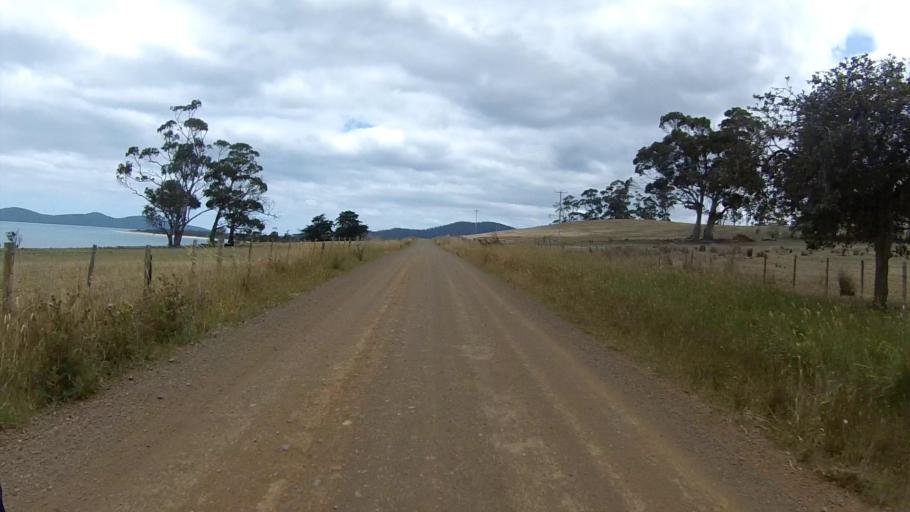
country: AU
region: Tasmania
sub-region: Sorell
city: Sorell
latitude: -42.6238
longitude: 147.9328
